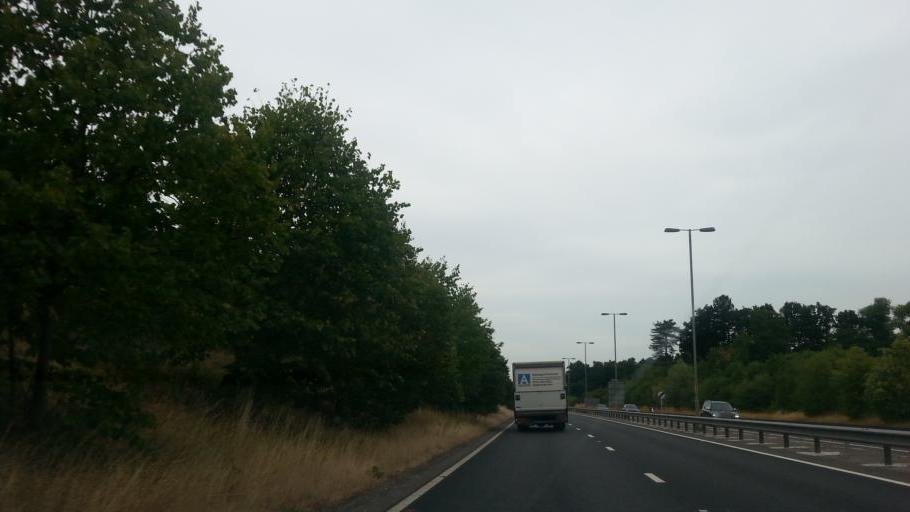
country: GB
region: England
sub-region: Derbyshire
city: Borrowash
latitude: 52.8880
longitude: -1.4059
